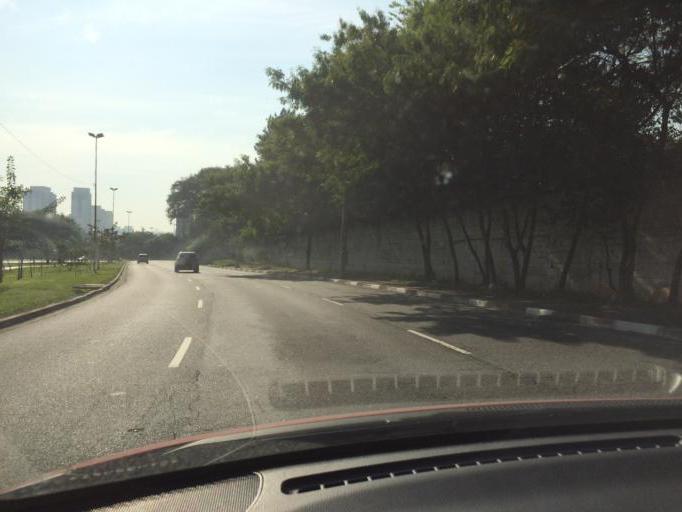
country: BR
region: Sao Paulo
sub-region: Osasco
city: Osasco
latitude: -23.5584
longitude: -46.7433
